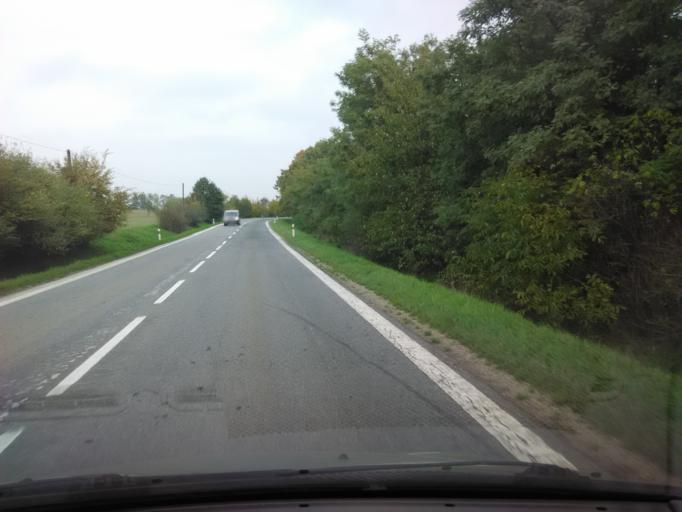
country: SK
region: Nitriansky
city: Svodin
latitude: 48.0356
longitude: 18.4241
